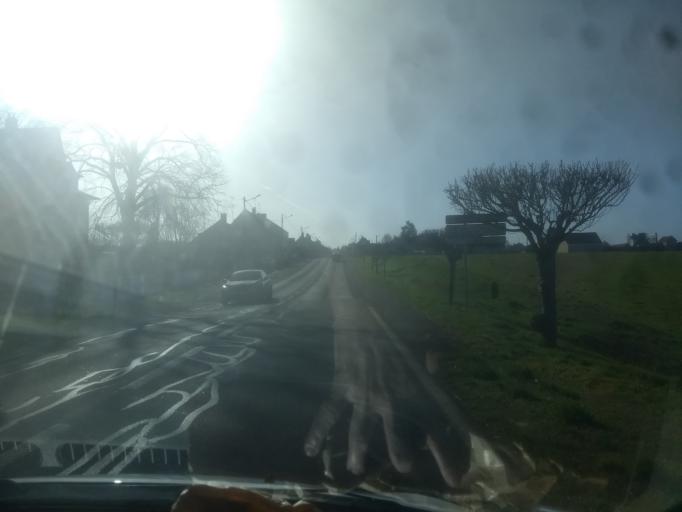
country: FR
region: Centre
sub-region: Departement du Cher
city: Orval
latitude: 46.7727
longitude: 2.4325
